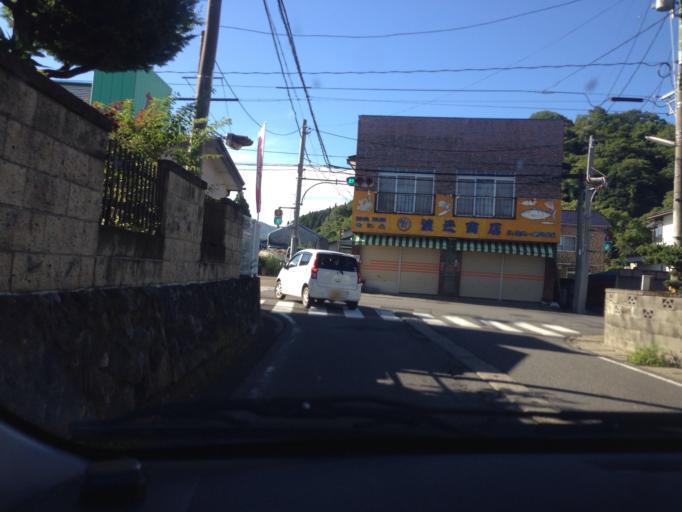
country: JP
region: Fukushima
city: Inawashiro
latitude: 37.3950
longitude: 140.1317
